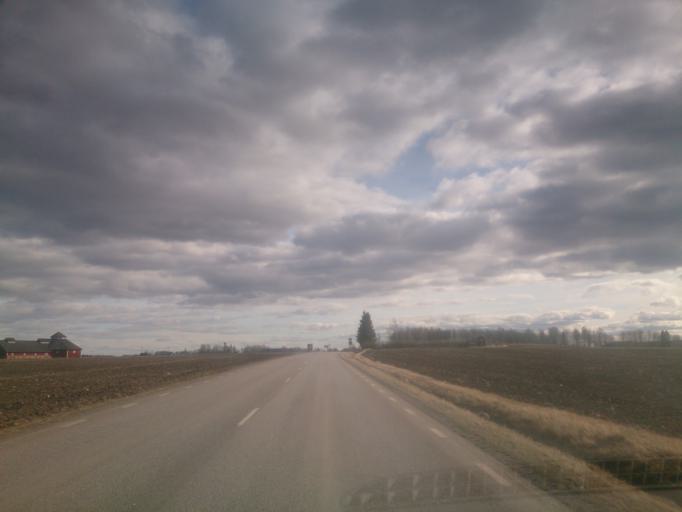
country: SE
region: OEstergoetland
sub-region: Motala Kommun
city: Borensberg
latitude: 58.5015
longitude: 15.2028
